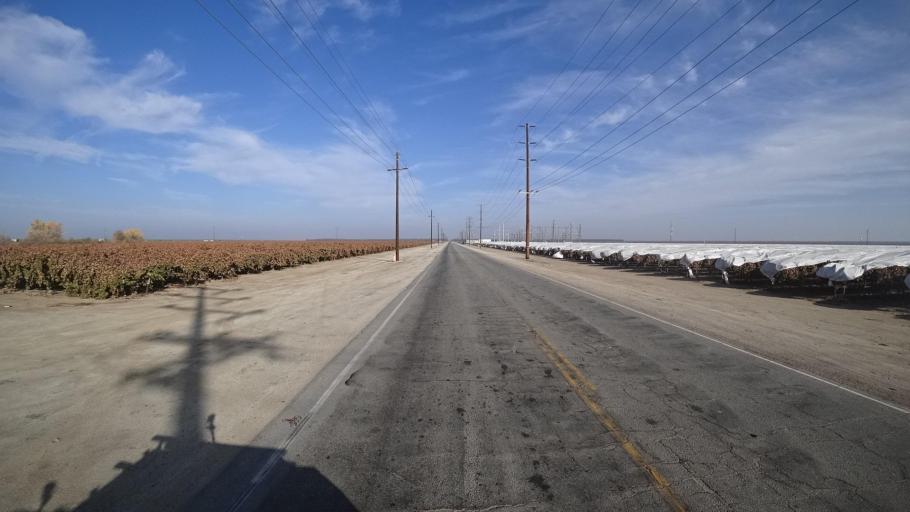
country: US
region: California
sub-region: Kern County
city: McFarland
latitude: 35.6023
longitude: -119.2043
